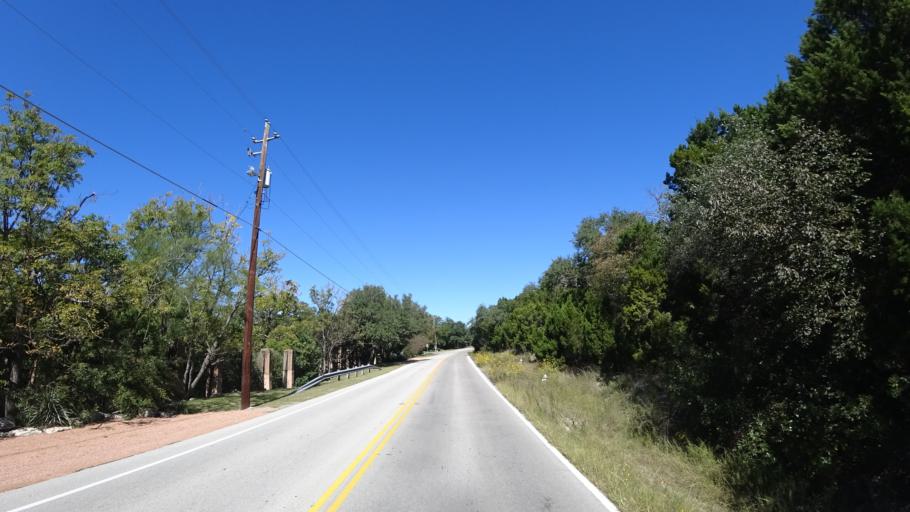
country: US
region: Texas
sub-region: Travis County
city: West Lake Hills
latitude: 30.3307
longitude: -97.7763
